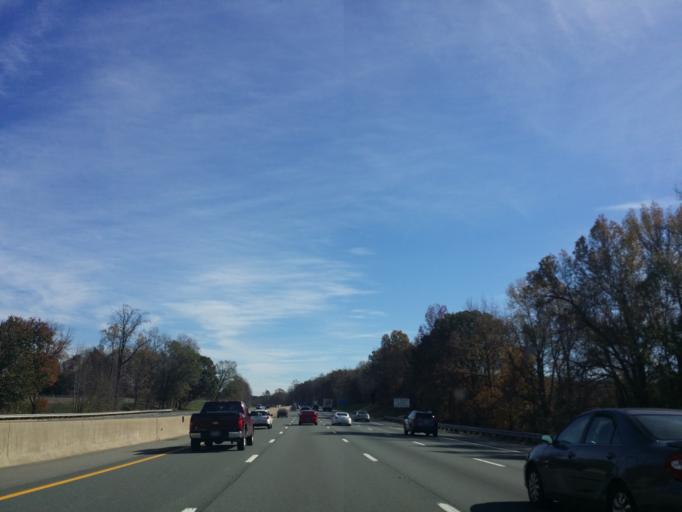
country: US
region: North Carolina
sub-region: Alamance County
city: Haw River
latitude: 36.0667
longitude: -79.3266
